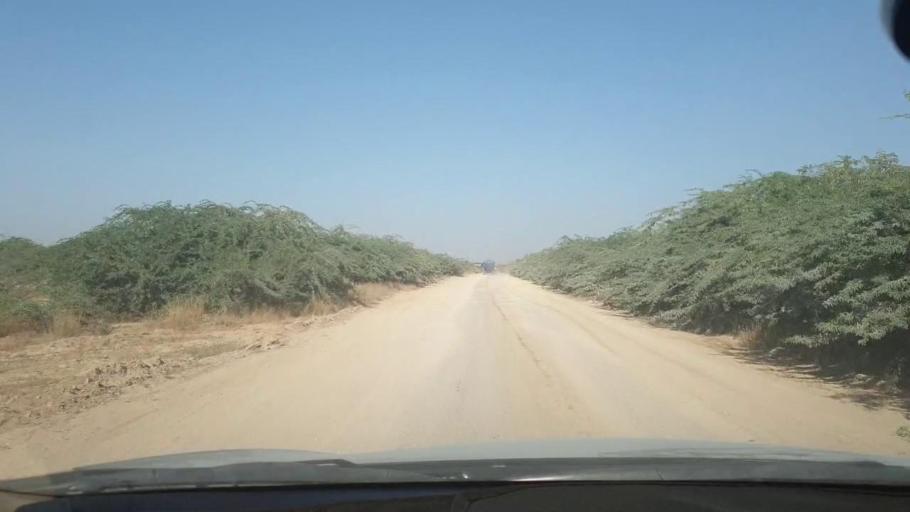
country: PK
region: Sindh
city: Malir Cantonment
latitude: 25.1431
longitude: 67.1651
